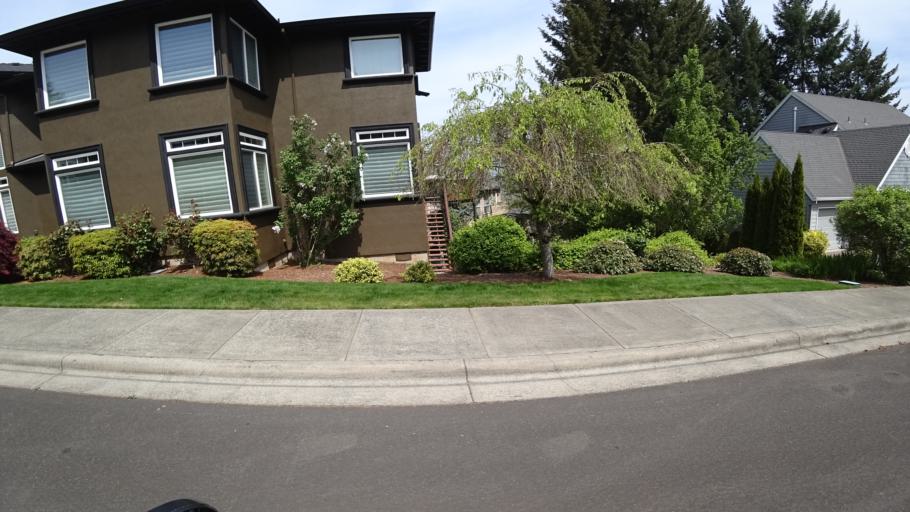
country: US
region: Oregon
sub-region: Washington County
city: Aloha
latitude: 45.4564
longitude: -122.8508
